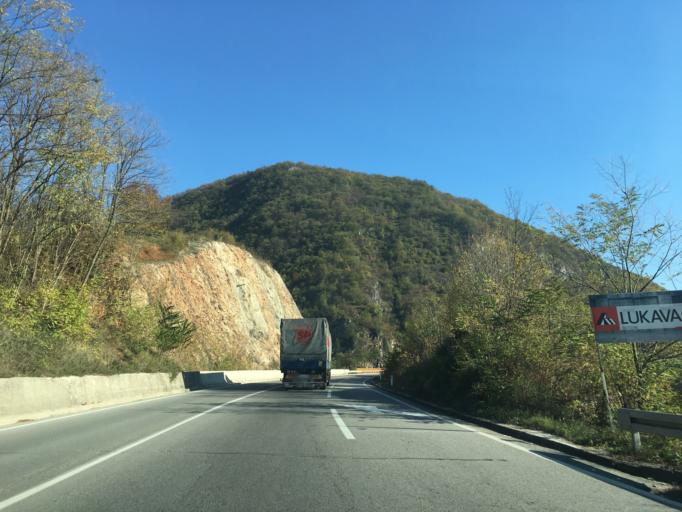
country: BA
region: Federation of Bosnia and Herzegovina
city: Kobilja Glava
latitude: 43.8538
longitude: 18.4613
